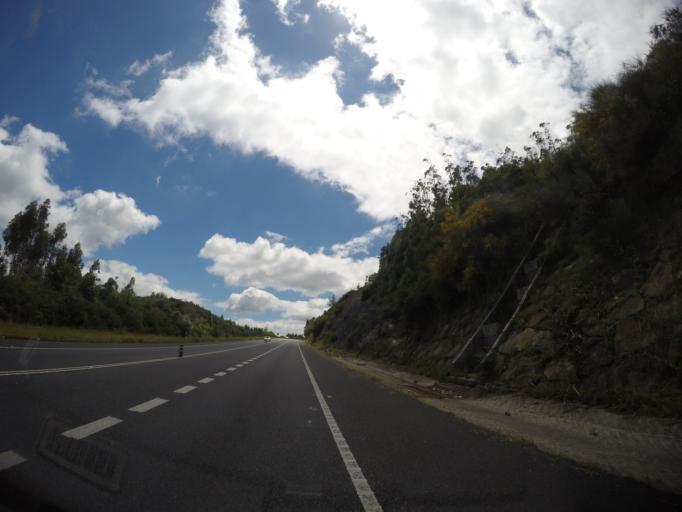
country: ES
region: Aragon
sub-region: Provincia de Zaragoza
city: El Burgo de Ebro
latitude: 41.5452
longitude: -0.7408
